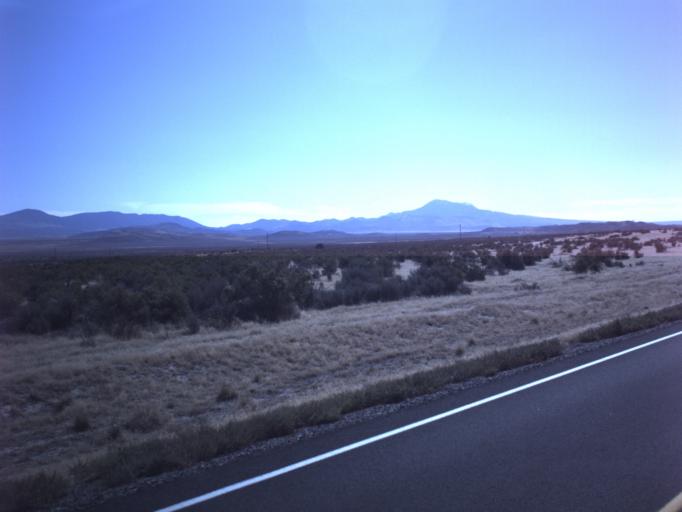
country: US
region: Utah
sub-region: Tooele County
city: Grantsville
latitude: 40.2420
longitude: -112.7232
